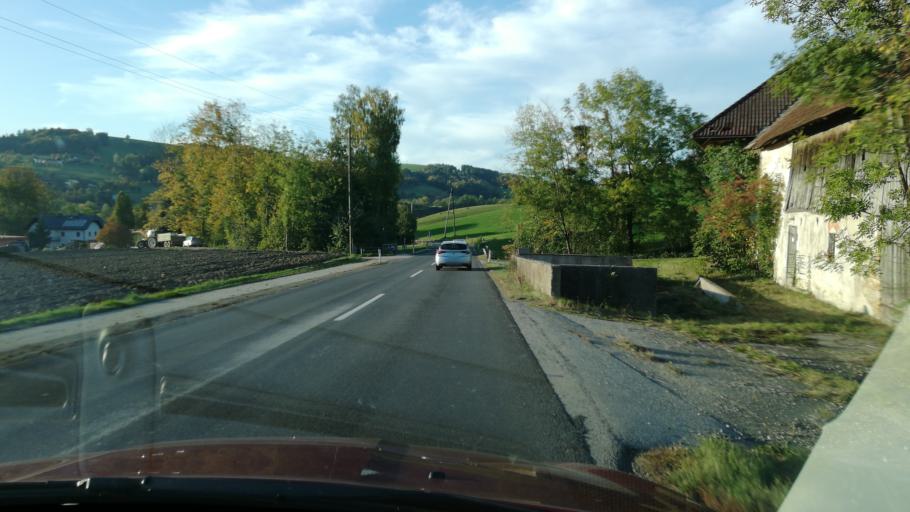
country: AT
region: Upper Austria
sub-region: Politischer Bezirk Kirchdorf an der Krems
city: Gruenburg
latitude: 47.9691
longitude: 14.2741
